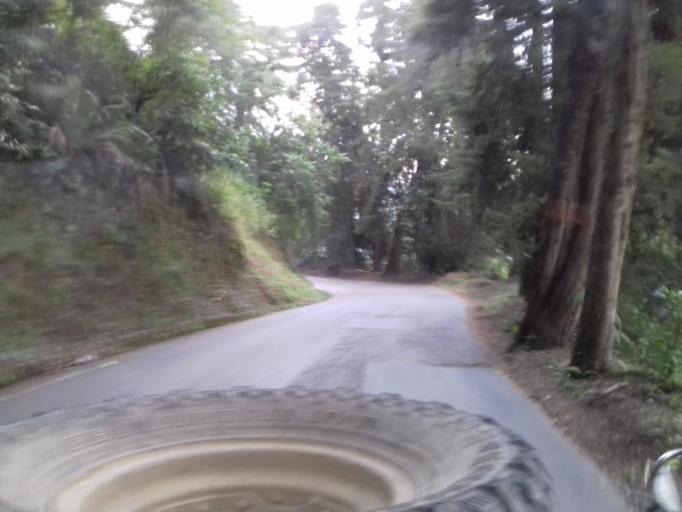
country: CO
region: Quindio
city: Salento
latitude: 4.6433
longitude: -75.5777
